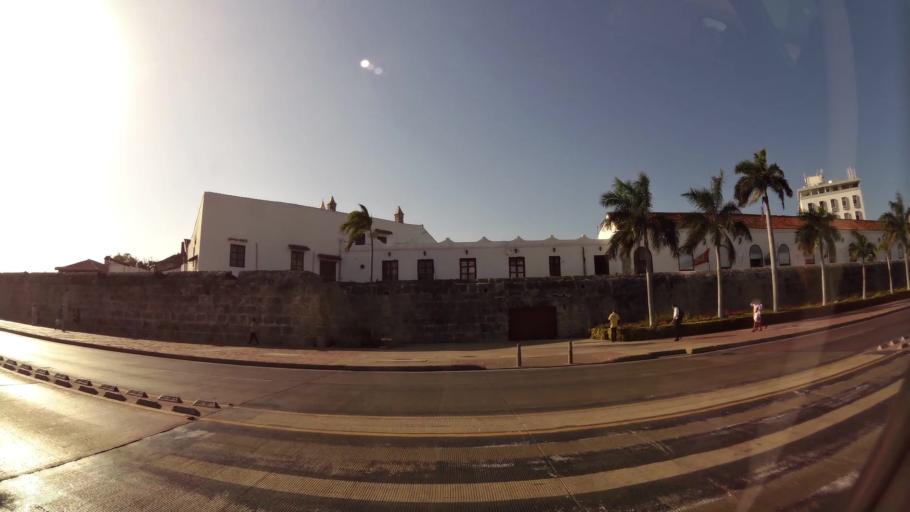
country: CO
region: Bolivar
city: Cartagena
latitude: 10.4214
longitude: -75.5500
